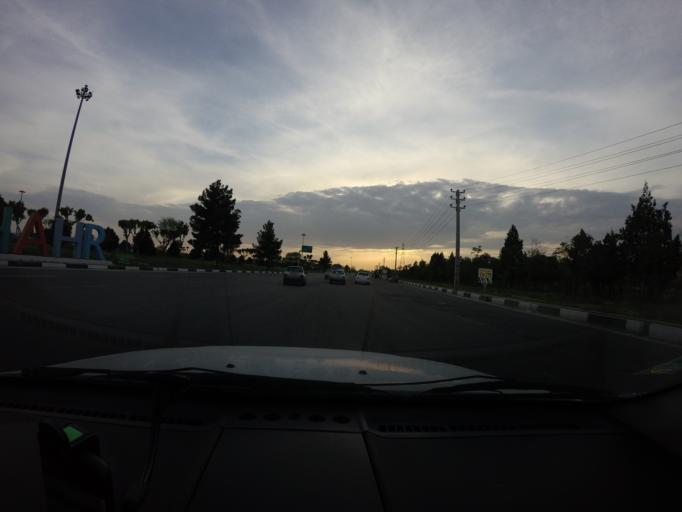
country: IR
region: Tehran
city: Eslamshahr
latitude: 35.5170
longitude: 51.2304
